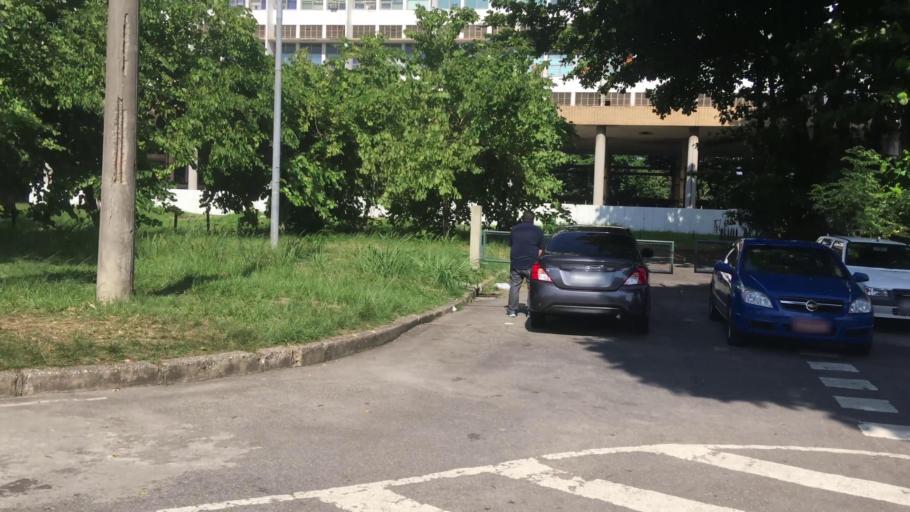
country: BR
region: Rio de Janeiro
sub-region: Rio De Janeiro
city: Rio de Janeiro
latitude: -22.8561
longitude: -43.2313
